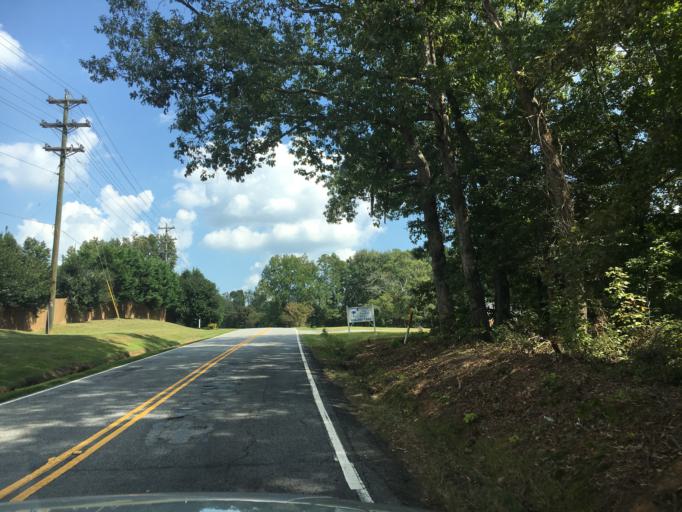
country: US
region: South Carolina
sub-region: Greenville County
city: Five Forks
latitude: 34.8298
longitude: -82.2613
